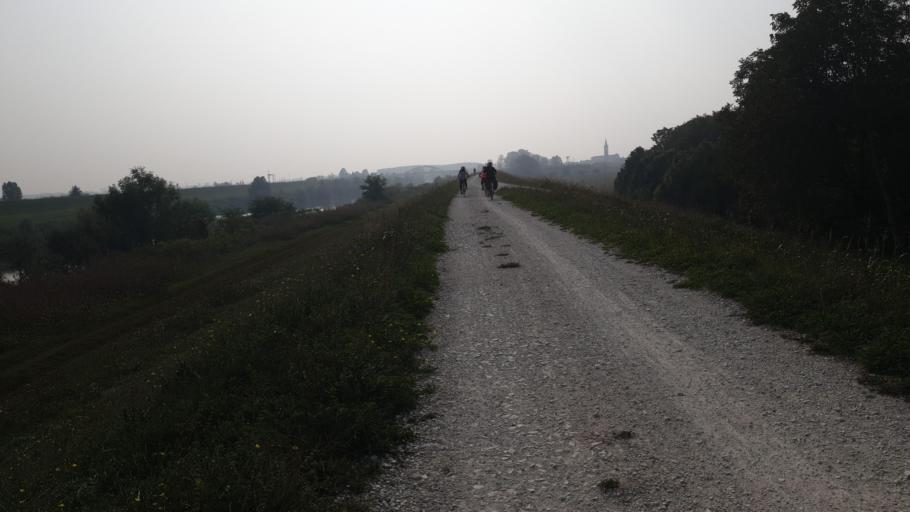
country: IT
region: Veneto
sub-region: Provincia di Padova
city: Corte
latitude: 45.3194
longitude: 12.0717
